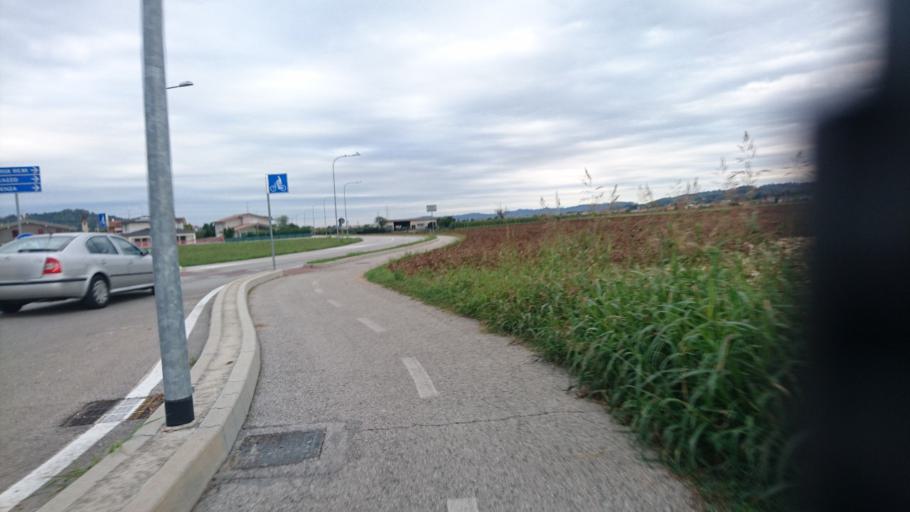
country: IT
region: Veneto
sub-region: Provincia di Vicenza
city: Sovizzo
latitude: 45.5193
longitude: 11.4336
